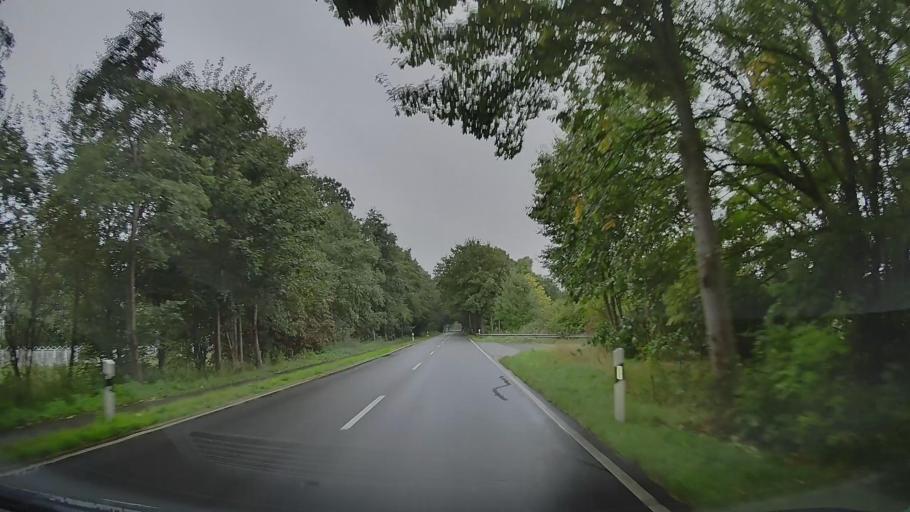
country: DE
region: Schleswig-Holstein
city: Buttel
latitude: 53.8980
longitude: 9.2052
